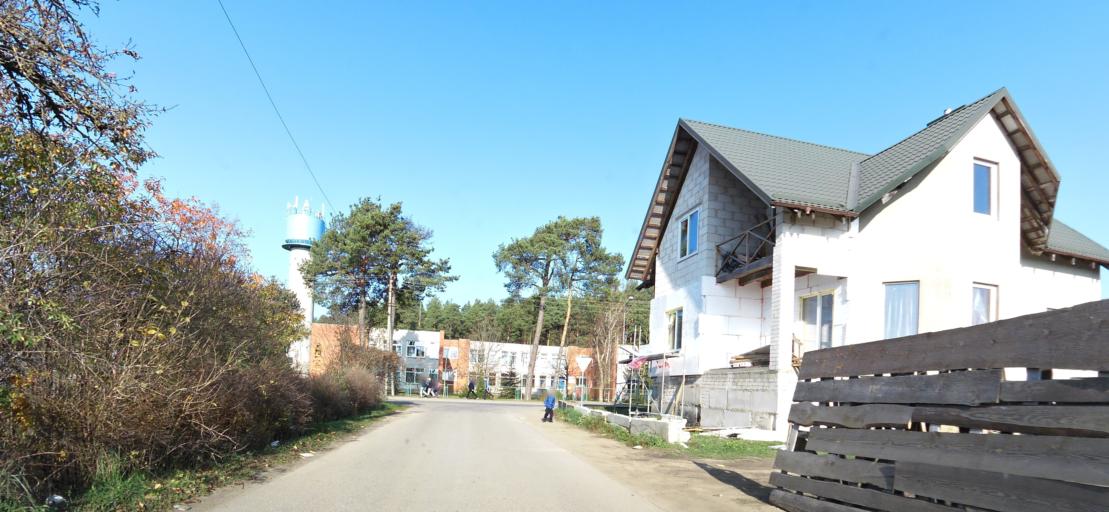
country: LT
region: Vilnius County
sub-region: Trakai
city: Rudiskes
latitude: 54.5142
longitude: 24.8230
